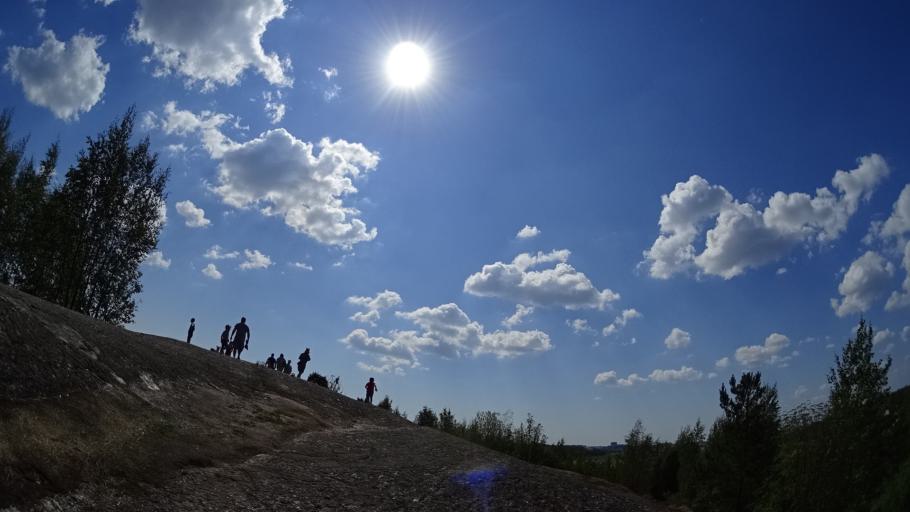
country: FI
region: Uusimaa
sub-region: Helsinki
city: Vantaa
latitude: 60.3388
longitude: 24.9945
